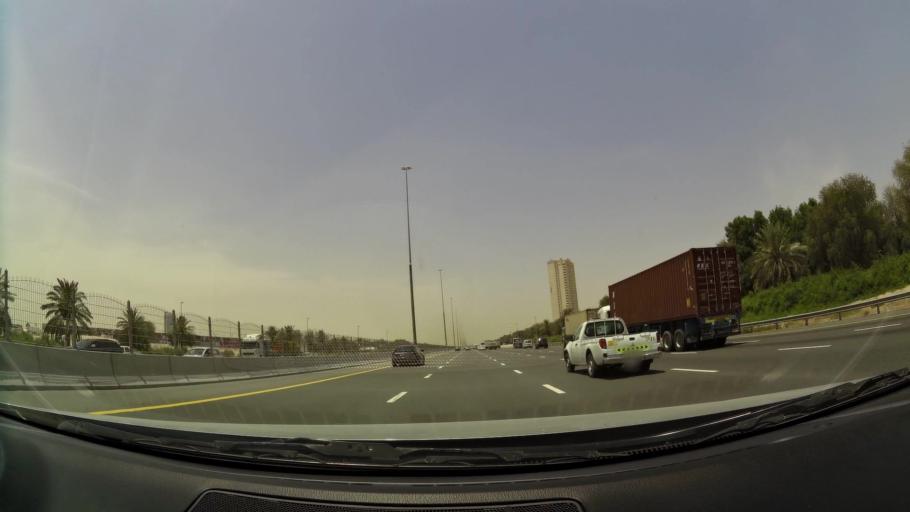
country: AE
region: Dubai
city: Dubai
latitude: 25.0966
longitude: 55.3295
